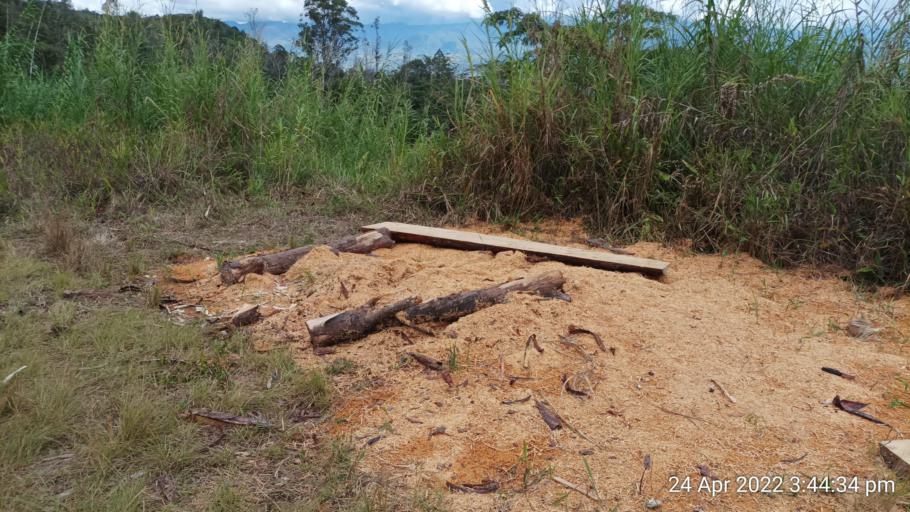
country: PG
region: Jiwaka
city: Minj
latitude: -5.8948
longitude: 144.8222
